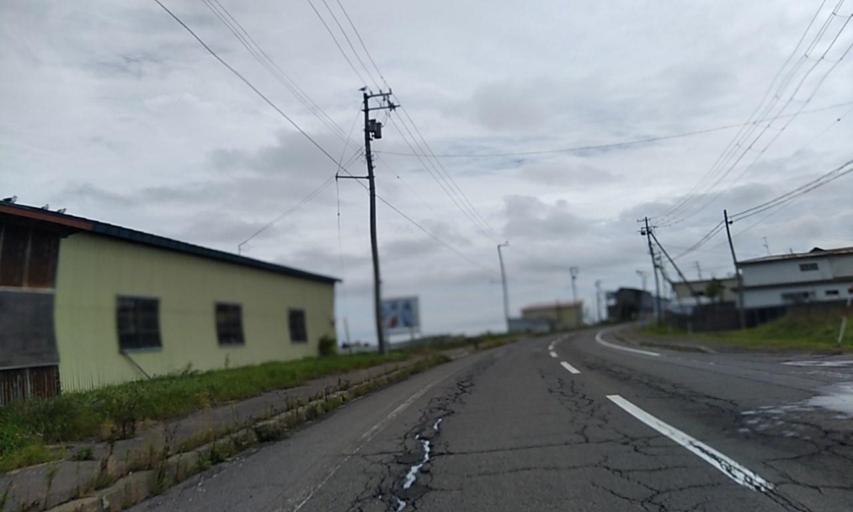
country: JP
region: Hokkaido
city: Shibetsu
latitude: 43.5761
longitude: 145.2153
